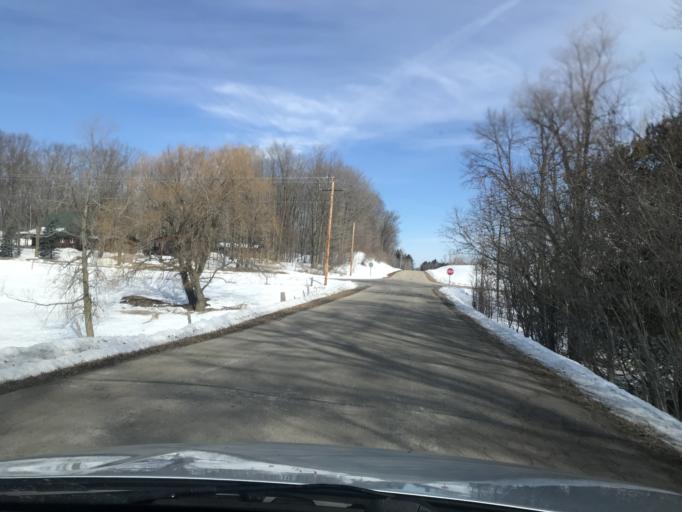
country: US
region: Wisconsin
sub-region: Oconto County
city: Gillett
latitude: 44.9684
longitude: -88.3061
